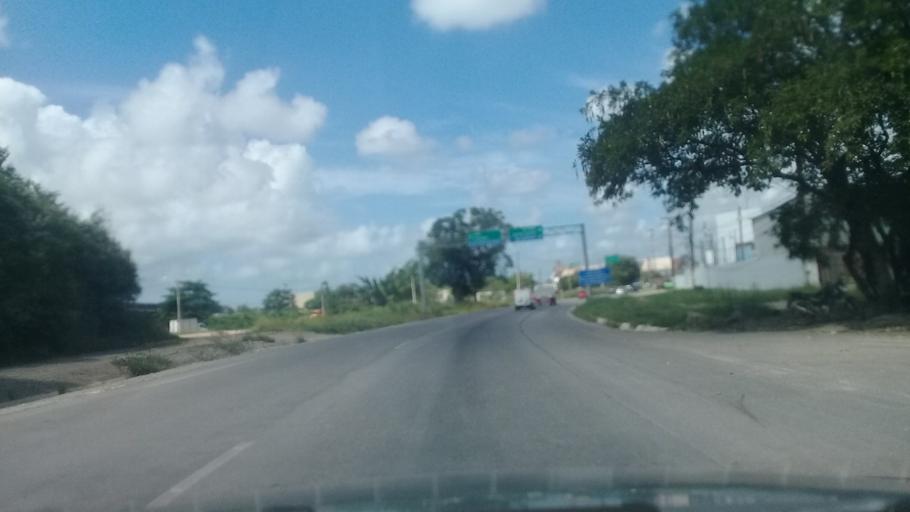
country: BR
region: Pernambuco
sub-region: Jaboatao Dos Guararapes
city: Jaboatao
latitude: -8.1688
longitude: -34.9380
